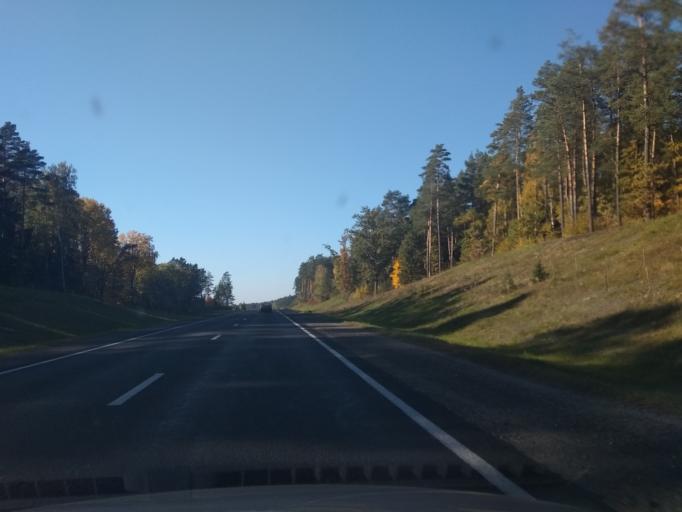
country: BY
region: Grodnenskaya
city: Zhyrovichy
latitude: 53.0484
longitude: 25.3485
